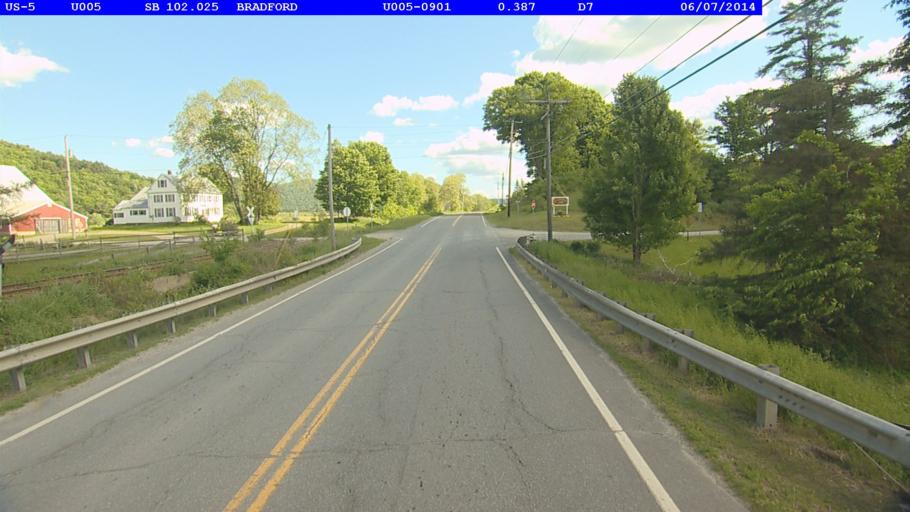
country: US
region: New Hampshire
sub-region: Grafton County
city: Orford
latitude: 43.9670
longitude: -72.1151
